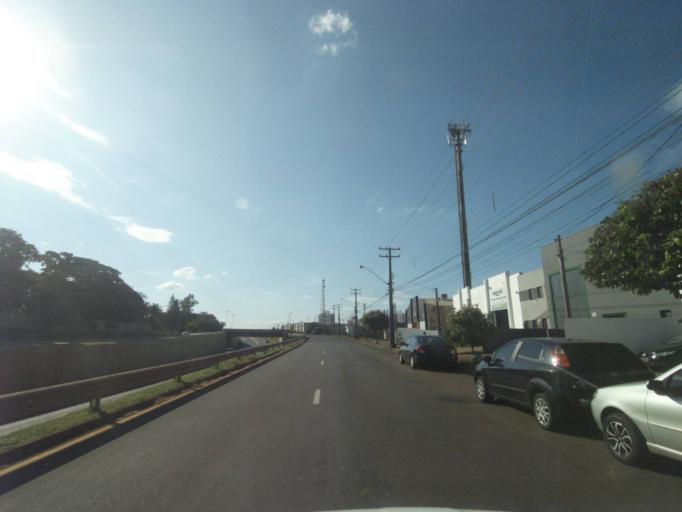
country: BR
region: Parana
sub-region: Londrina
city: Londrina
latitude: -23.3504
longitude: -51.1657
